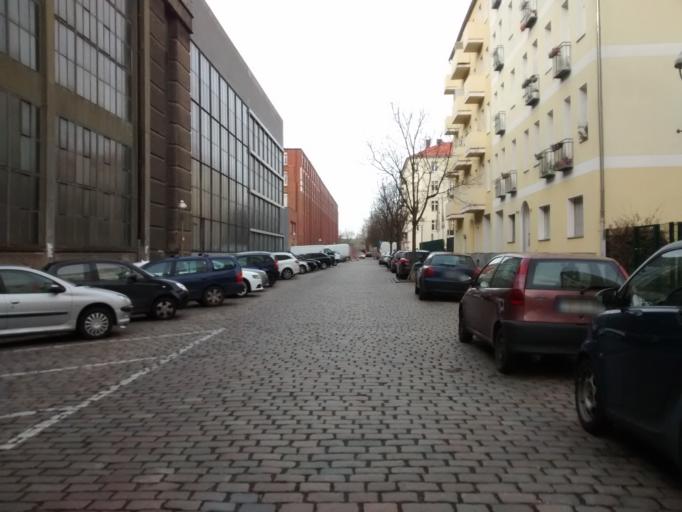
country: DE
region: Berlin
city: Moabit
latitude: 52.5299
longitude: 13.3249
